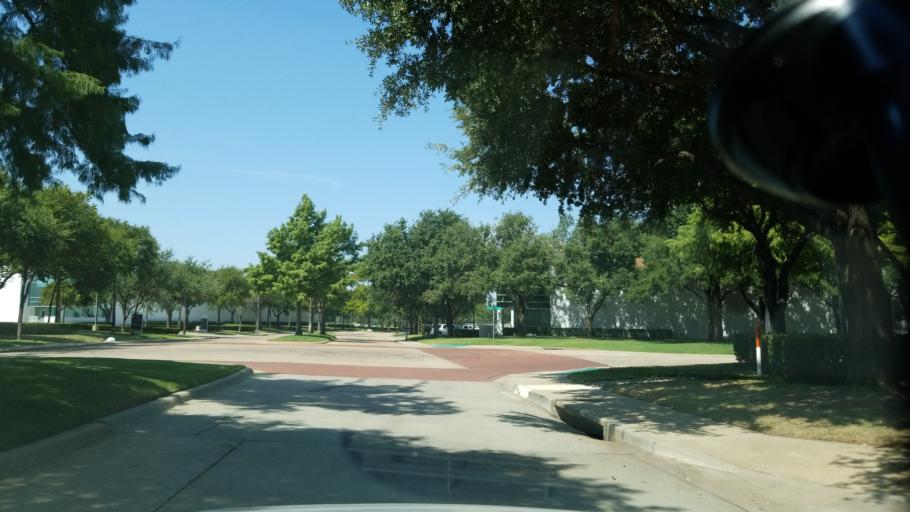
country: US
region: Texas
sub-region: Dallas County
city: Farmers Branch
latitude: 32.9040
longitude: -96.9039
